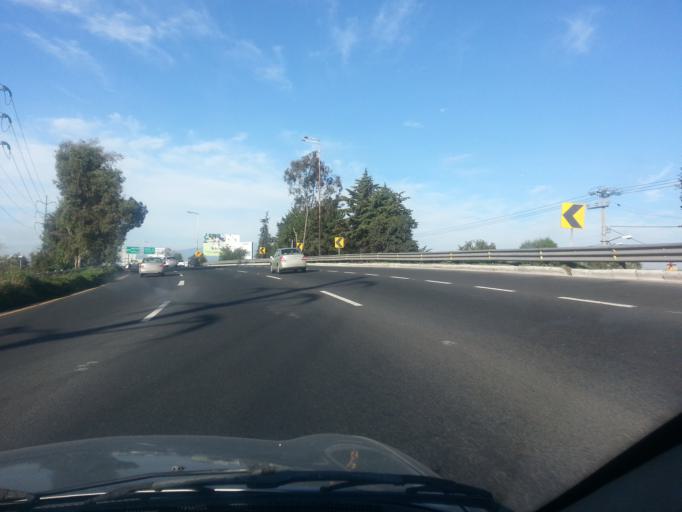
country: MX
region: Morelos
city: Lerma de Villada
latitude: 19.2833
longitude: -99.5078
